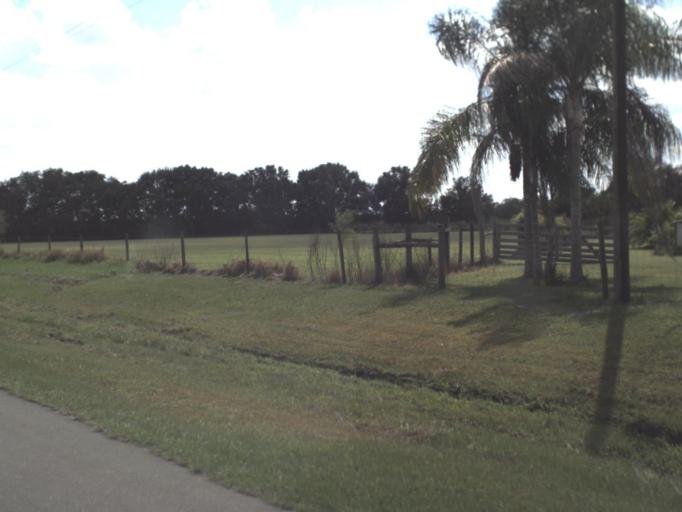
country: US
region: Florida
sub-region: Hardee County
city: Zolfo Springs
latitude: 27.4731
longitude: -81.7133
